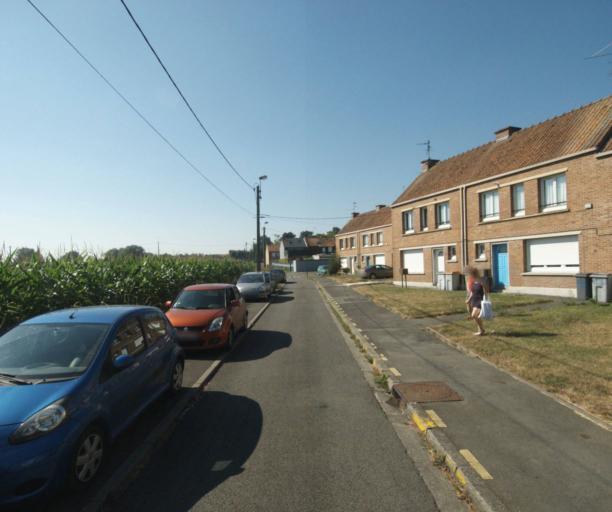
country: FR
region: Nord-Pas-de-Calais
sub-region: Departement du Nord
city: Wervicq-Sud
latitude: 50.7699
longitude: 3.0560
